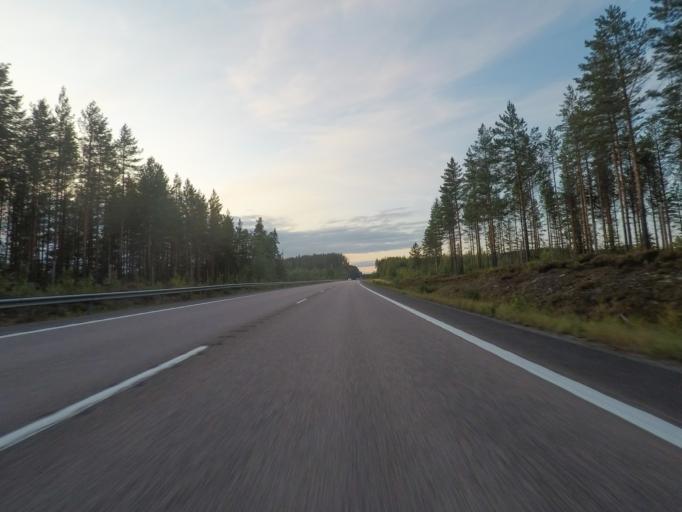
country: FI
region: Central Finland
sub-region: Jyvaeskylae
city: Saeynaetsalo
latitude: 62.2015
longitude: 25.8913
